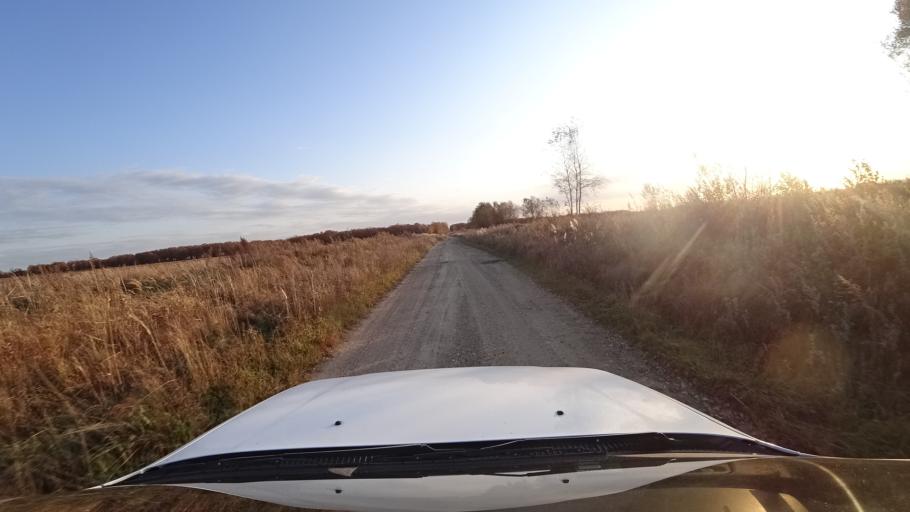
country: RU
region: Primorskiy
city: Lazo
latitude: 45.8103
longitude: 133.6078
